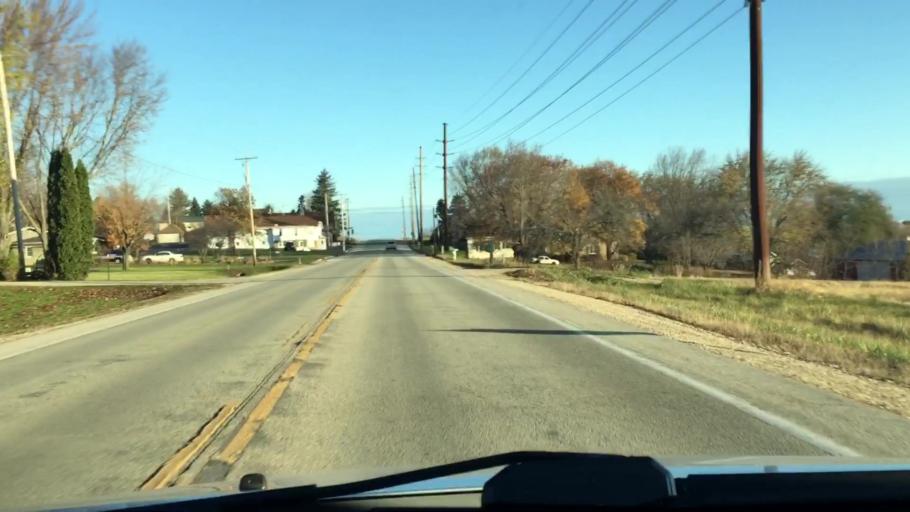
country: US
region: Wisconsin
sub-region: Washington County
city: Hartford
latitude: 43.3827
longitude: -88.4608
